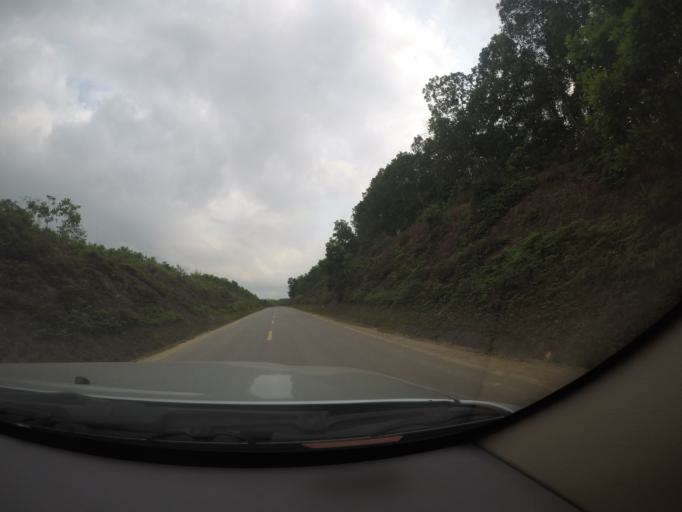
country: VN
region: Quang Tri
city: Ho Xa
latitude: 17.0673
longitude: 106.8604
